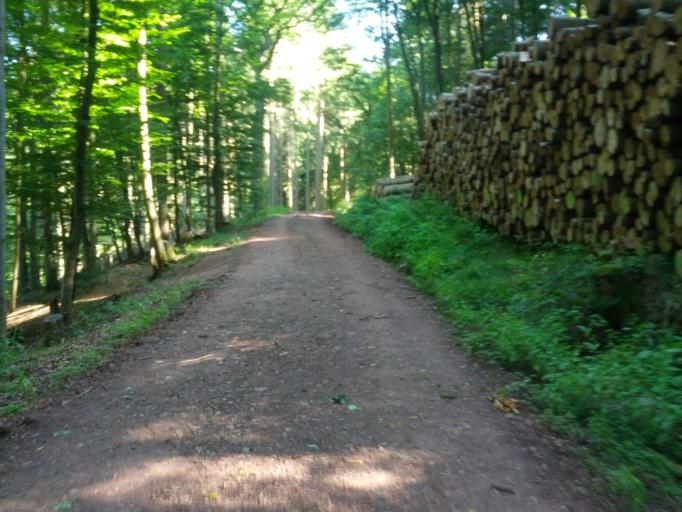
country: DE
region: Thuringia
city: Eisenach
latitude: 50.9463
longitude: 10.3070
